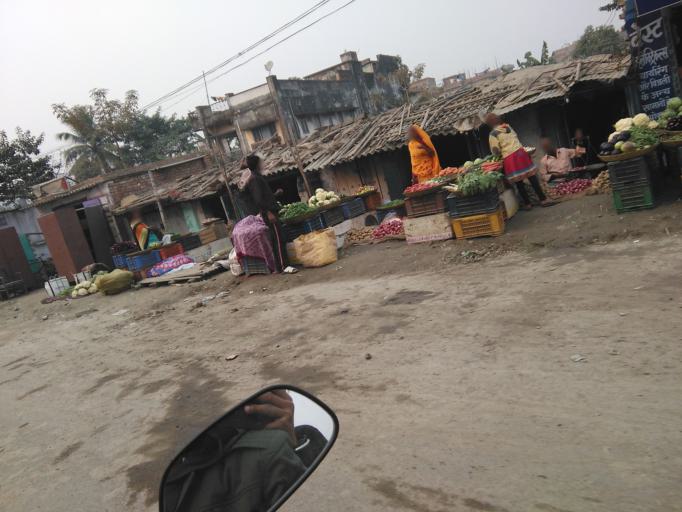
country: IN
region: Bihar
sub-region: Muzaffarpur
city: Muzaffarpur
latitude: 26.1069
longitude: 85.3911
